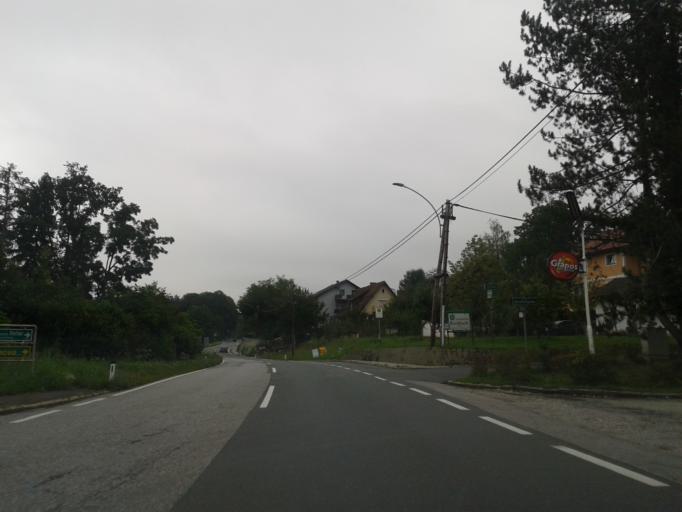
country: AT
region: Styria
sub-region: Graz Stadt
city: Mariatrost
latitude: 47.0910
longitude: 15.5115
